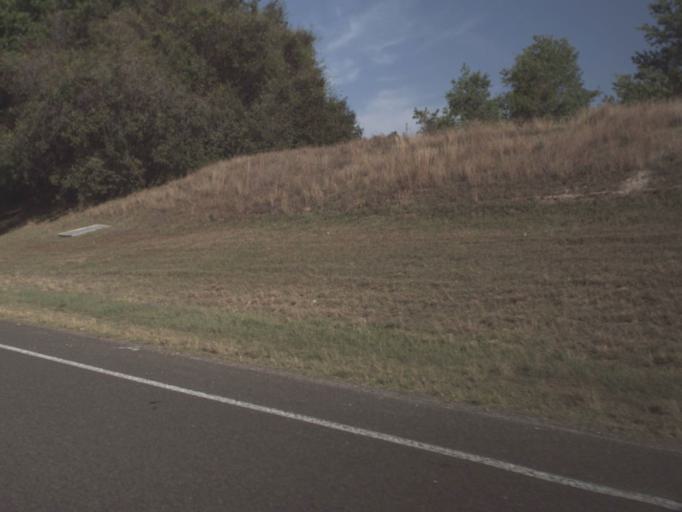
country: US
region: Florida
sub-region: Lake County
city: Howie In The Hills
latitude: 28.6437
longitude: -81.8118
